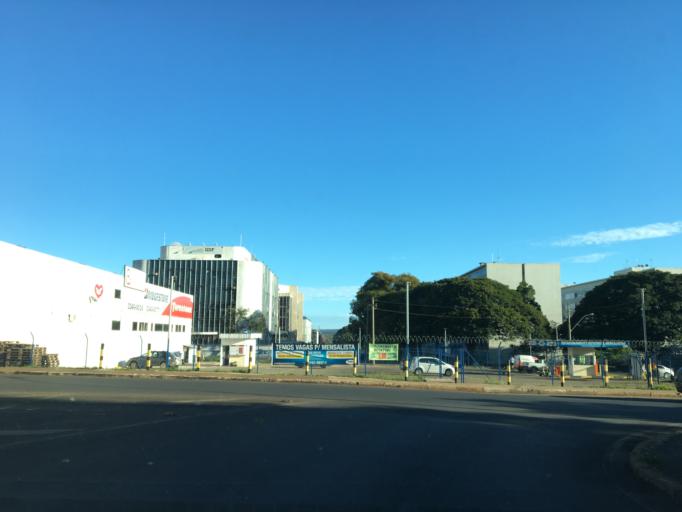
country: BR
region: Federal District
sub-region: Brasilia
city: Brasilia
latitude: -15.7449
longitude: -47.8964
